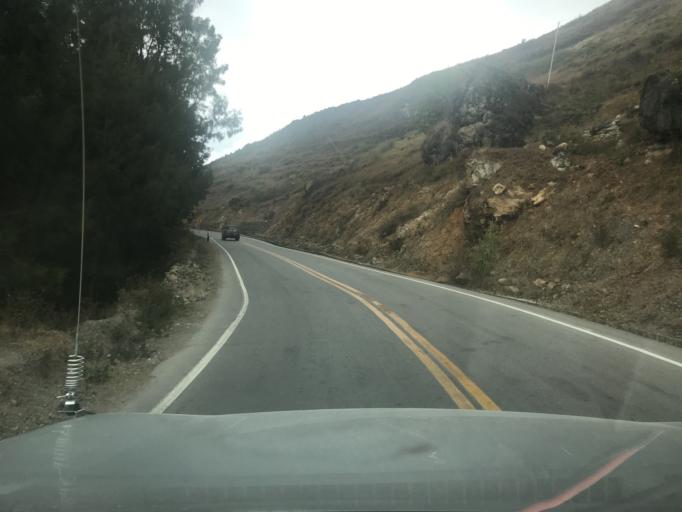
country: TL
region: Manufahi
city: Same
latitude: -8.8874
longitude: 125.5999
